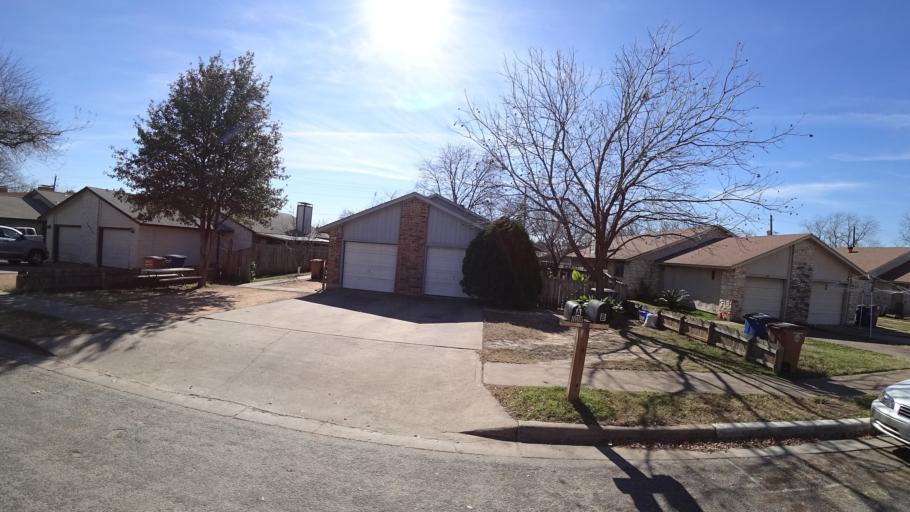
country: US
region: Texas
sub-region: Travis County
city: Wells Branch
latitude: 30.3716
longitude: -97.6977
